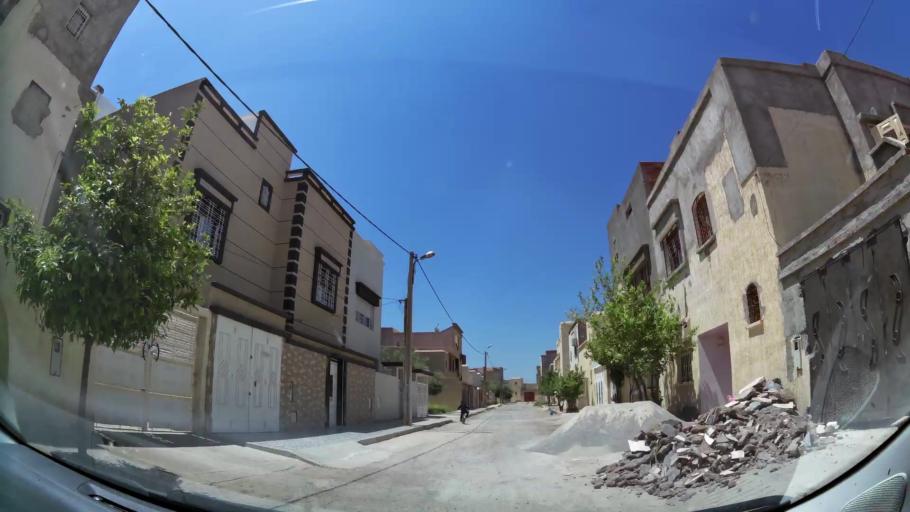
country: MA
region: Oriental
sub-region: Oujda-Angad
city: Oujda
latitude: 34.6668
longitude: -1.9444
